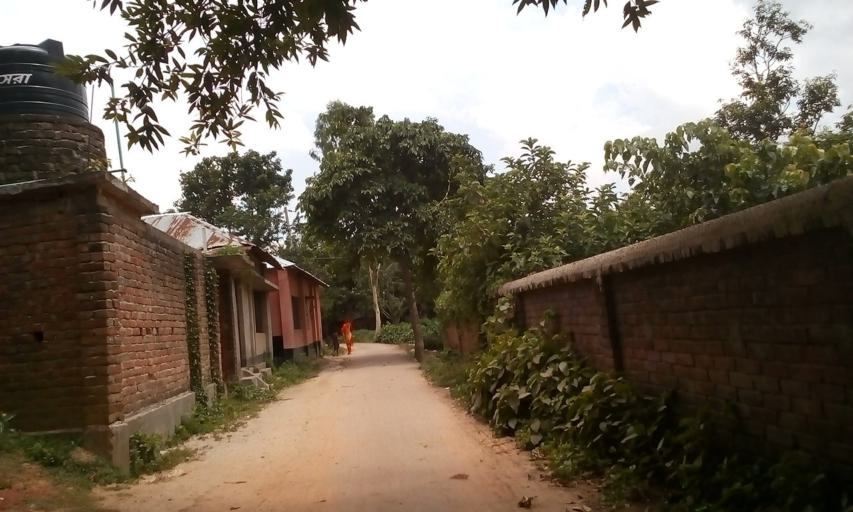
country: IN
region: West Bengal
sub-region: Dakshin Dinajpur
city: Balurghat
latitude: 25.3829
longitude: 88.9966
